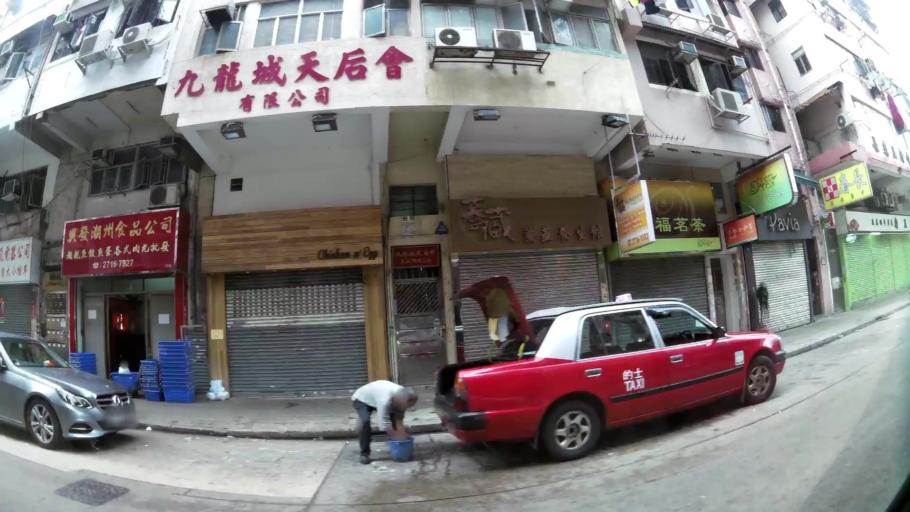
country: HK
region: Kowloon City
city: Kowloon
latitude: 22.3301
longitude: 114.1915
